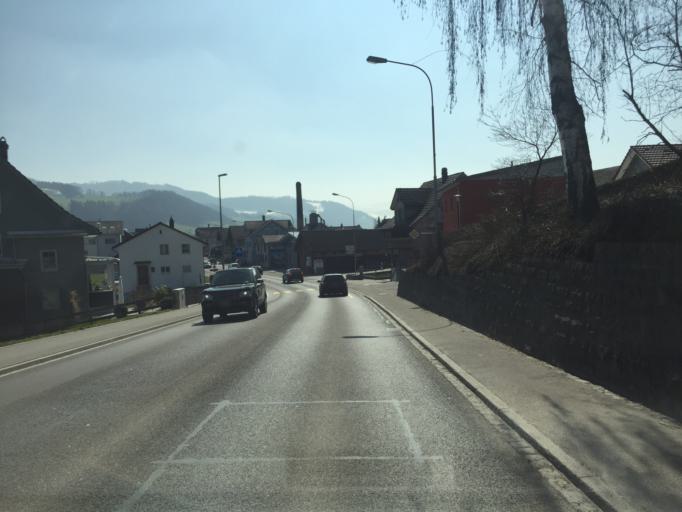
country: CH
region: Saint Gallen
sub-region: Wahlkreis Toggenburg
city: Buetschwil
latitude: 47.3530
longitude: 9.0748
